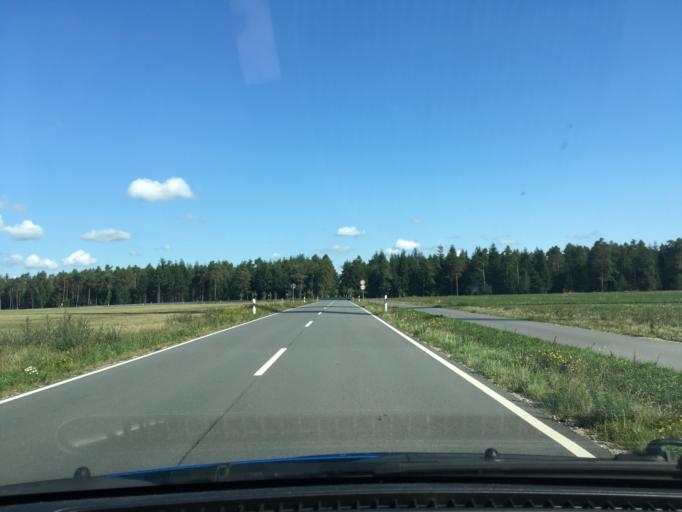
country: DE
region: Lower Saxony
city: Wietzendorf
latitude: 52.8879
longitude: 10.0361
